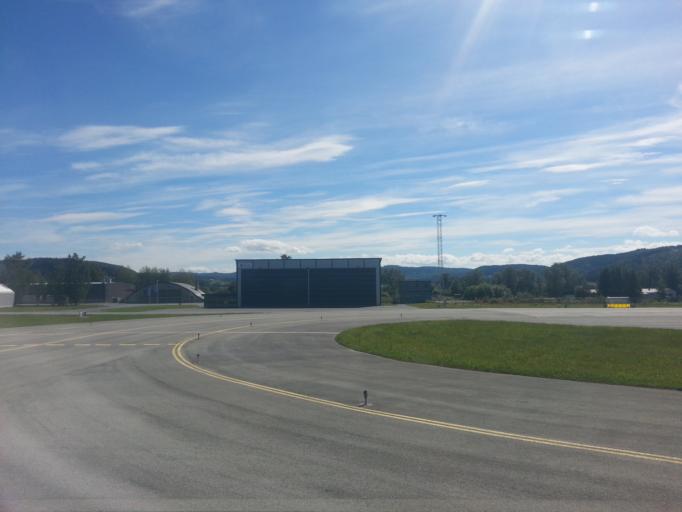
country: NO
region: Nord-Trondelag
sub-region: Stjordal
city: Stjordalshalsen
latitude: 63.4560
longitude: 10.9336
